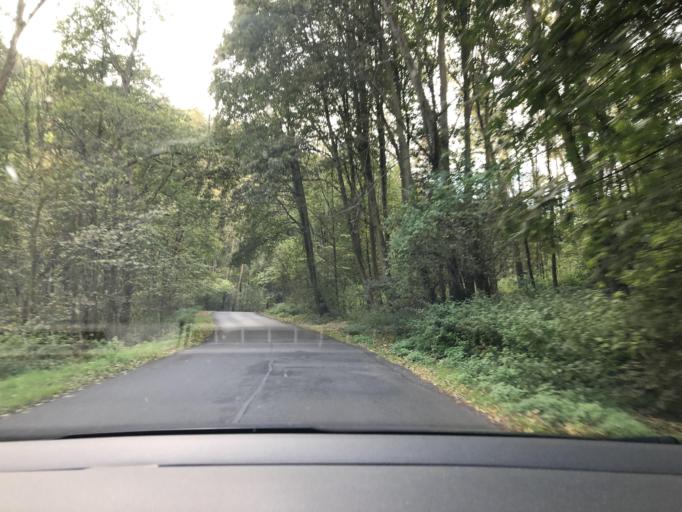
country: CZ
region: Ustecky
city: Velke Brezno
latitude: 50.6462
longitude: 14.1460
